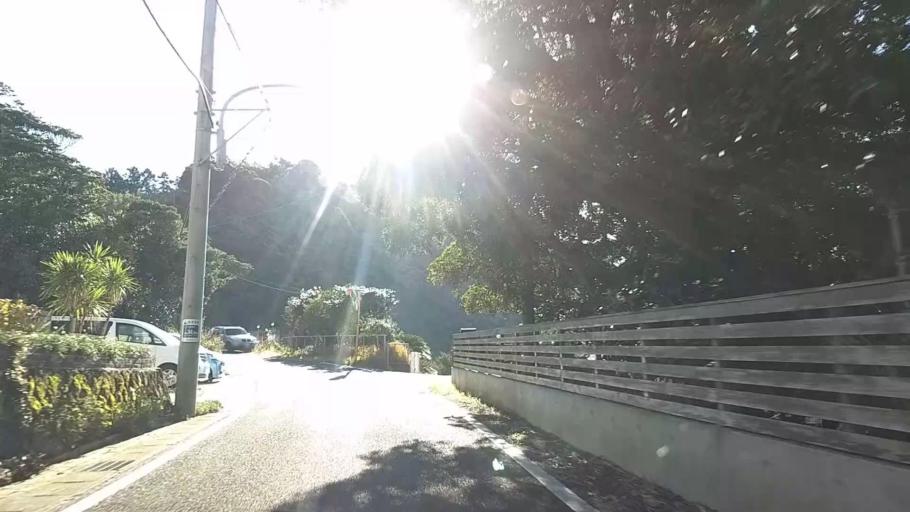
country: JP
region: Chiba
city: Futtsu
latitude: 35.2441
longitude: 139.8696
